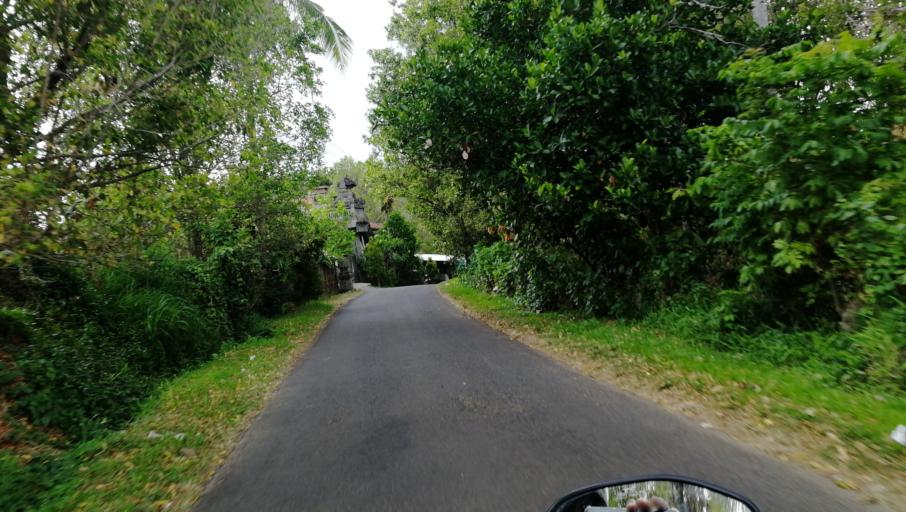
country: ID
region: Bali
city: Banjar Pedawa
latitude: -8.2798
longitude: 115.0339
